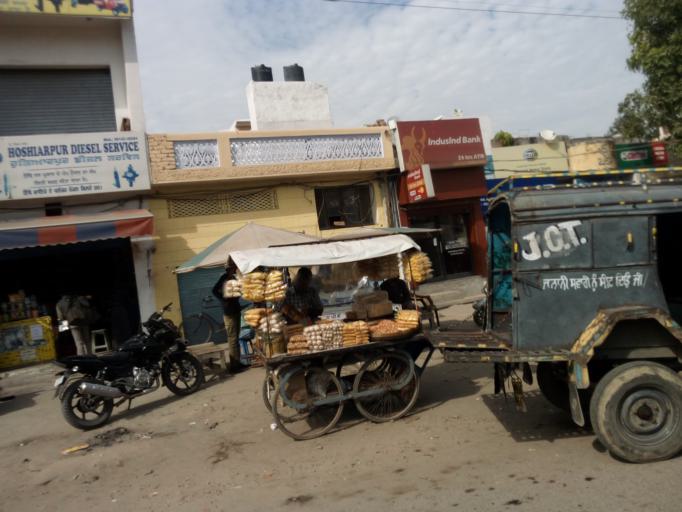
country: IN
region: Punjab
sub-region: Hoshiarpur
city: Hoshiarpur
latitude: 31.5333
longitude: 75.9022
